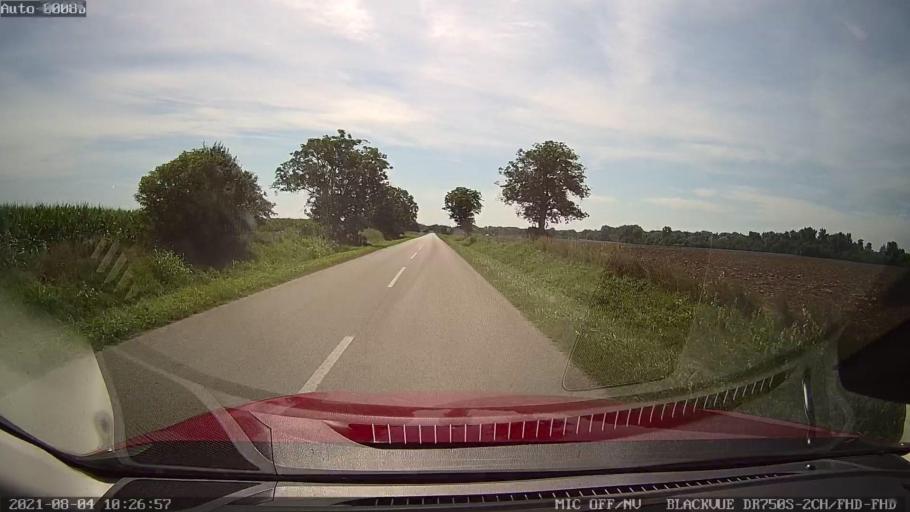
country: HR
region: Osjecko-Baranjska
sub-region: Grad Osijek
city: Bilje
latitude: 45.6033
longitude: 18.7715
